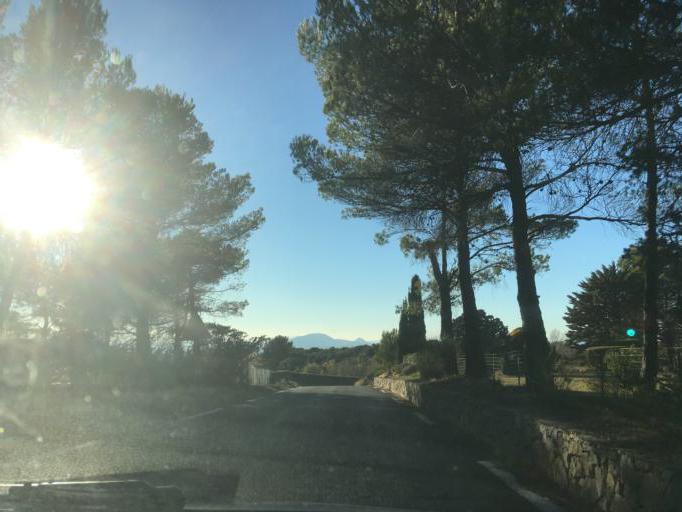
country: FR
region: Provence-Alpes-Cote d'Azur
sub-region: Departement du Var
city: Villecroze
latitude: 43.5920
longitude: 6.3103
